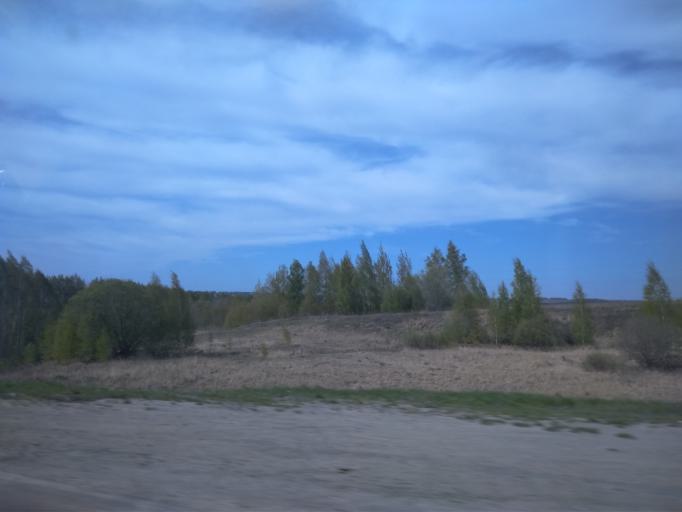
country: RU
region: Mordoviya
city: Chamzinka
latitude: 54.3640
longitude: 45.6212
